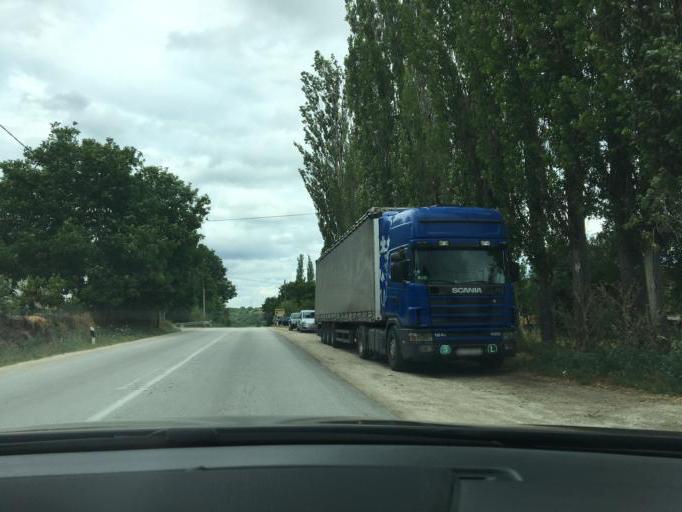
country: MK
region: Kriva Palanka
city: Kriva Palanka
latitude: 42.1765
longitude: 22.2530
